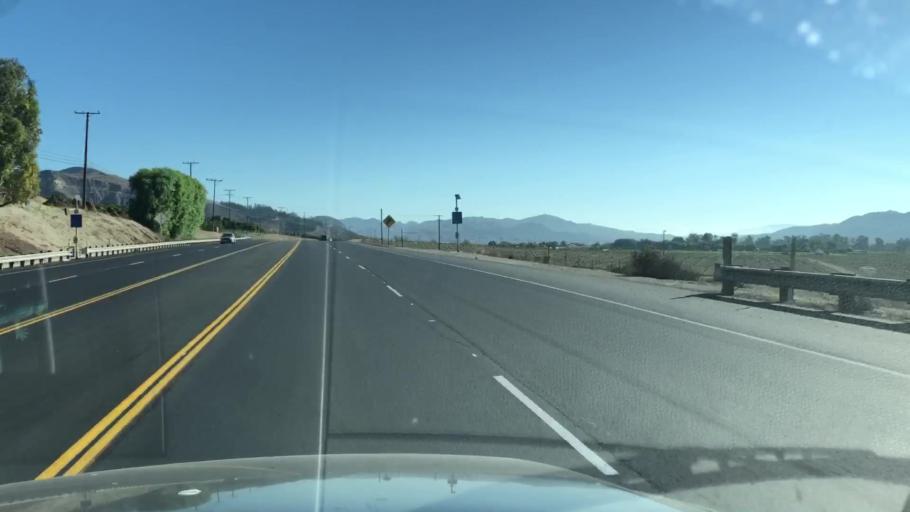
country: US
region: California
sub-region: Ventura County
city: Piru
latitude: 34.3988
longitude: -118.8431
